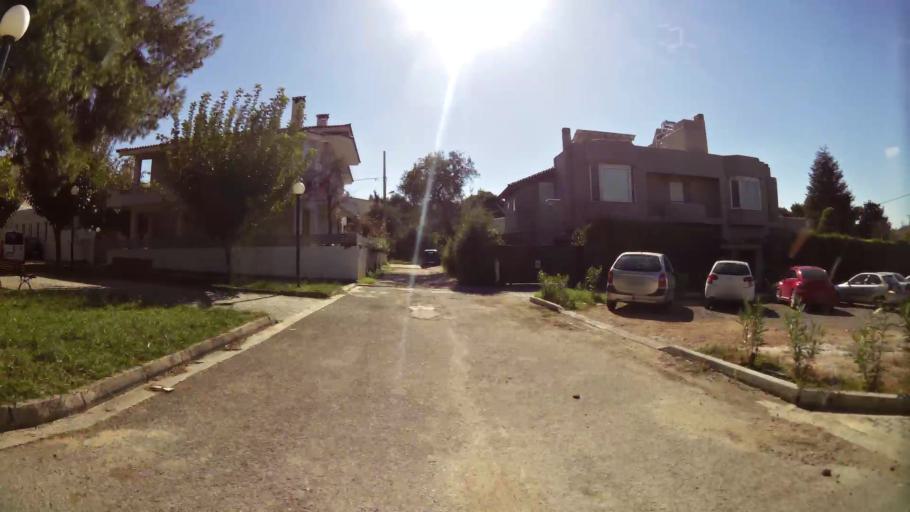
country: GR
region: Attica
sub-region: Nomarchia Athinas
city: Nea Erythraia
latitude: 38.1016
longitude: 23.8245
